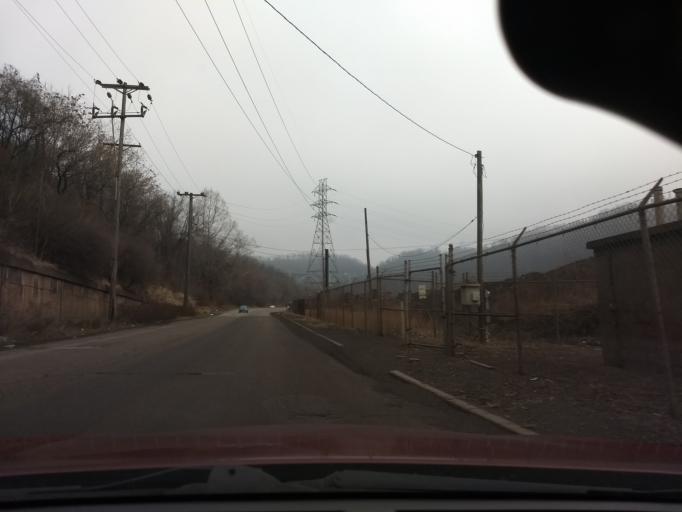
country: US
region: Pennsylvania
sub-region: Allegheny County
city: North Braddock
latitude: 40.3938
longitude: -79.8458
